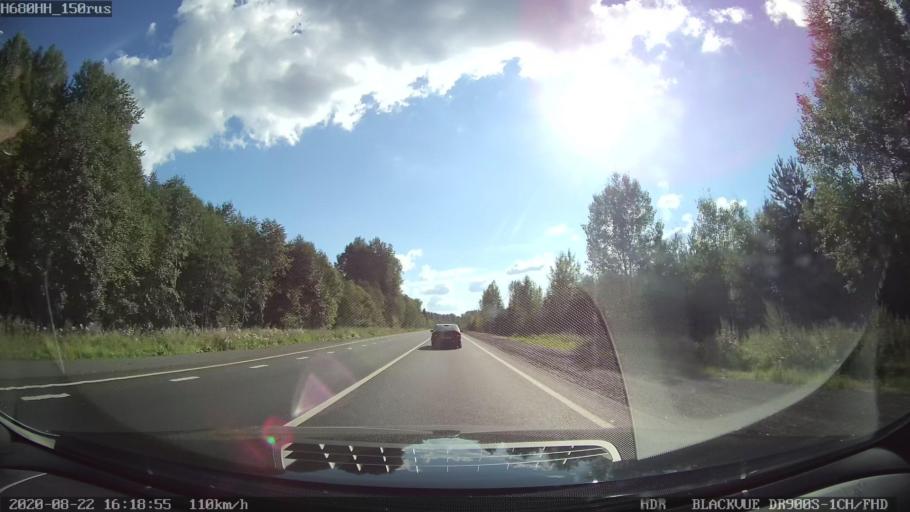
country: RU
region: Tverskaya
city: Rameshki
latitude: 57.4101
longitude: 36.1296
